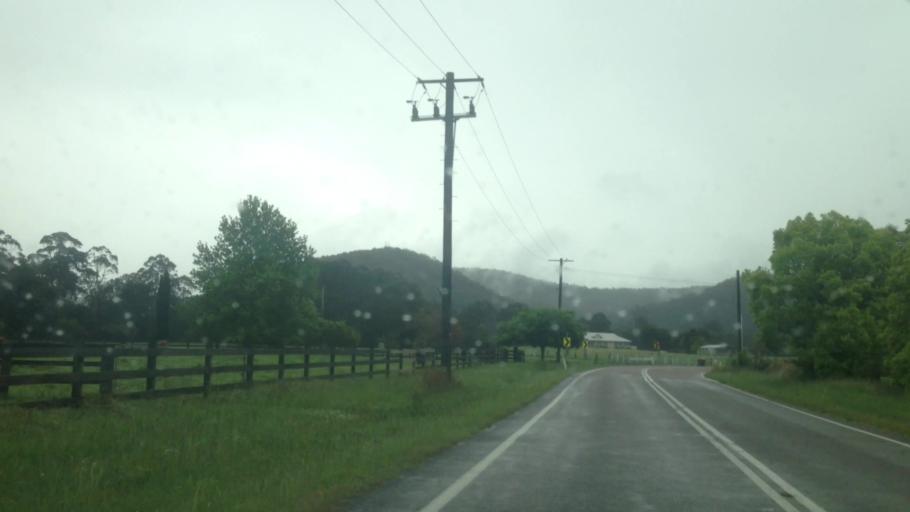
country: AU
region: New South Wales
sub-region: Wyong Shire
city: Little Jilliby
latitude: -33.2351
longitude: 151.3769
